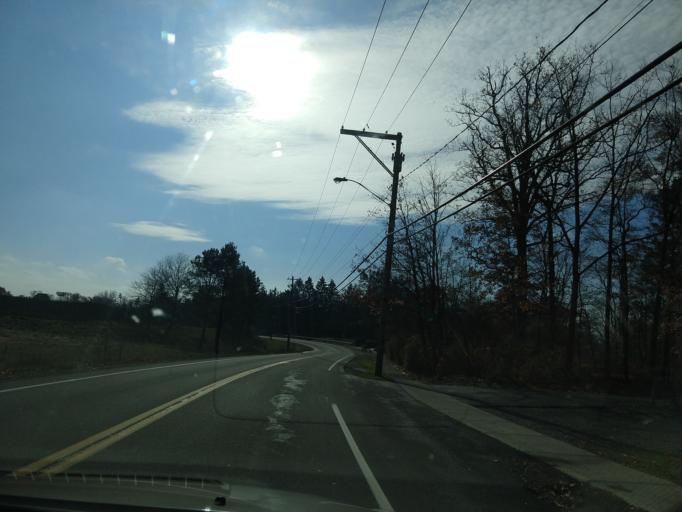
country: US
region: New York
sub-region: Tompkins County
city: Cayuga Heights
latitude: 42.4593
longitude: -76.4819
